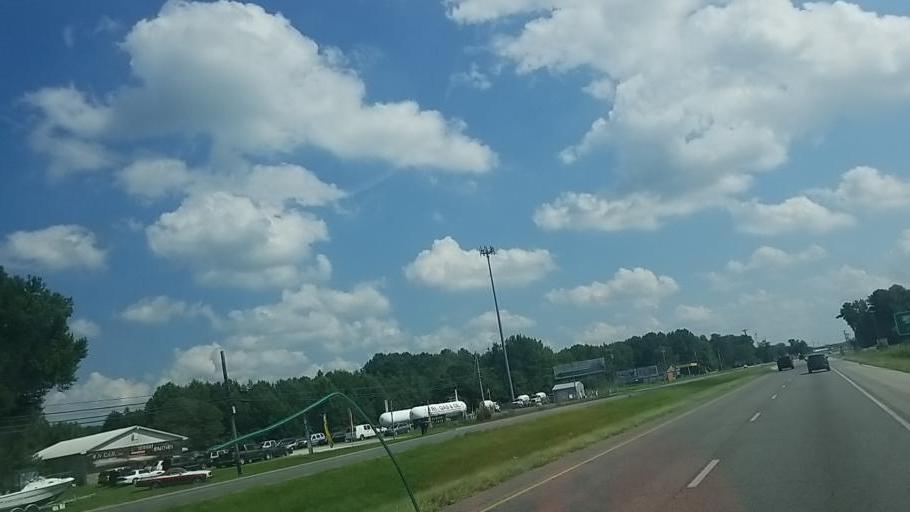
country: US
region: Delaware
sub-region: Sussex County
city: Georgetown
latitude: 38.7097
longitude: -75.4048
